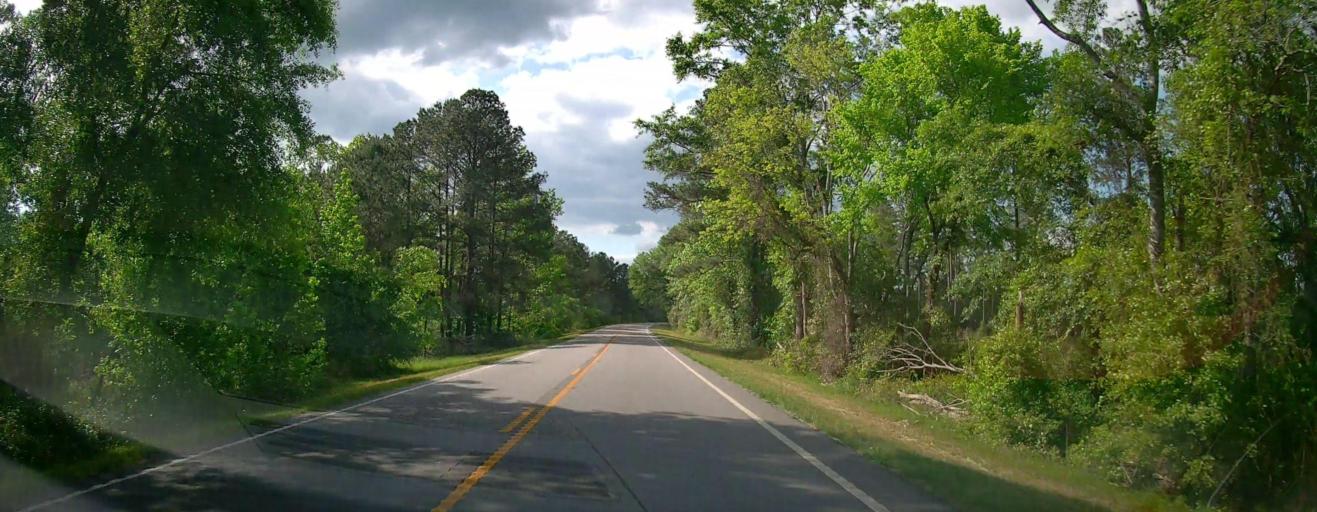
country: US
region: Georgia
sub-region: Baldwin County
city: Hardwick
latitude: 33.0451
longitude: -83.1191
